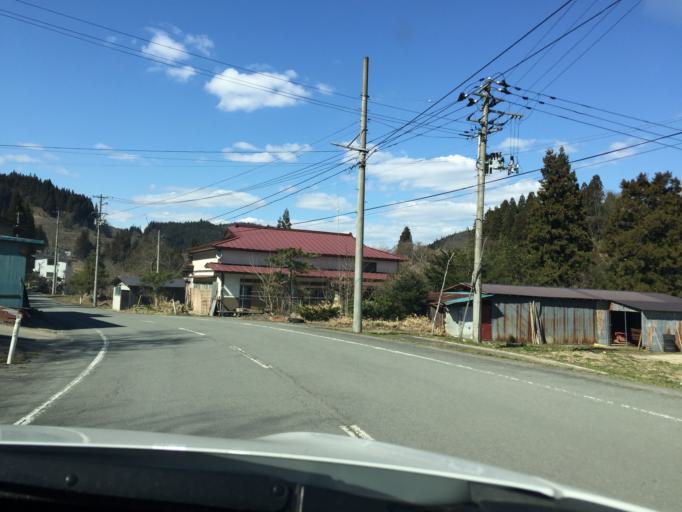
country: JP
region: Yamagata
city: Nagai
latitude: 38.2519
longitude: 140.1048
